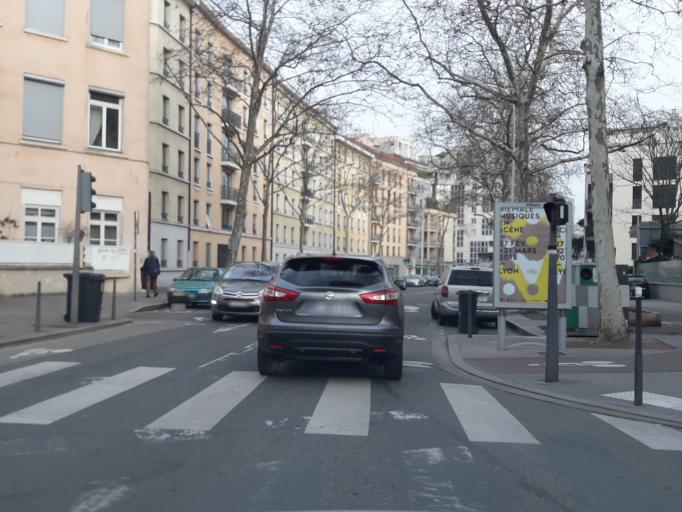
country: FR
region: Rhone-Alpes
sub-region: Departement du Rhone
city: Caluire-et-Cuire
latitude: 45.7783
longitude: 4.8280
